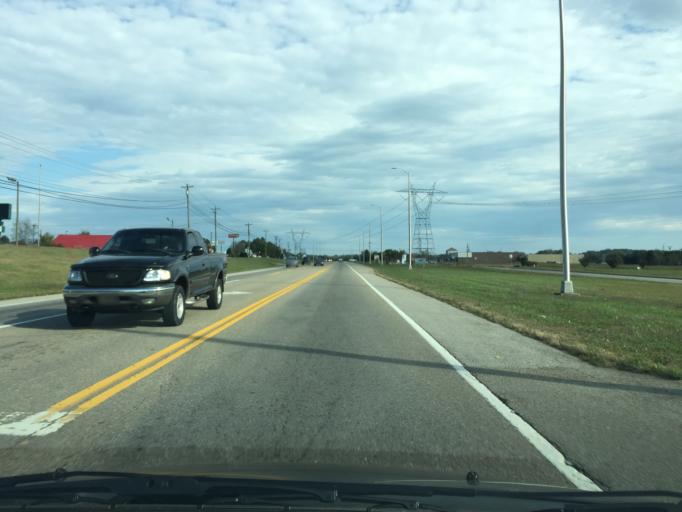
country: US
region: Tennessee
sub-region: Loudon County
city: Loudon
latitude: 35.7204
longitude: -84.3684
